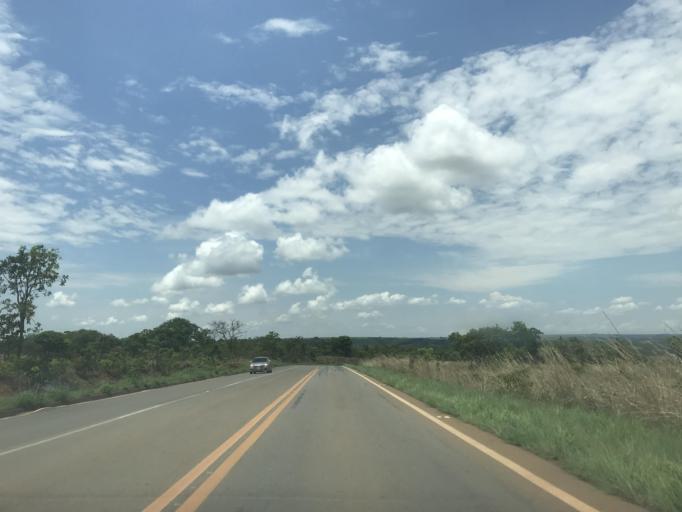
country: BR
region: Goias
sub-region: Luziania
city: Luziania
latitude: -16.3982
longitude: -48.1710
